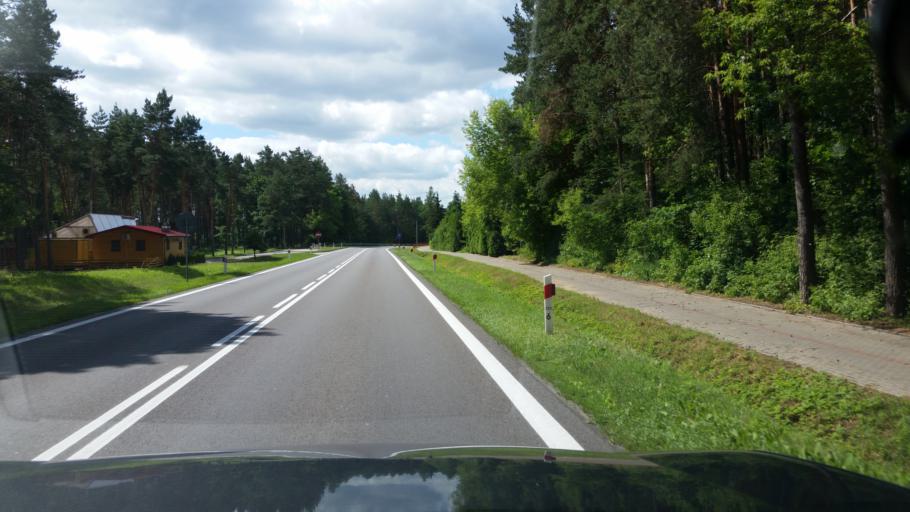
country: PL
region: Podlasie
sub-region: Powiat grajewski
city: Rajgrod
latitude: 53.7097
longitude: 22.6710
